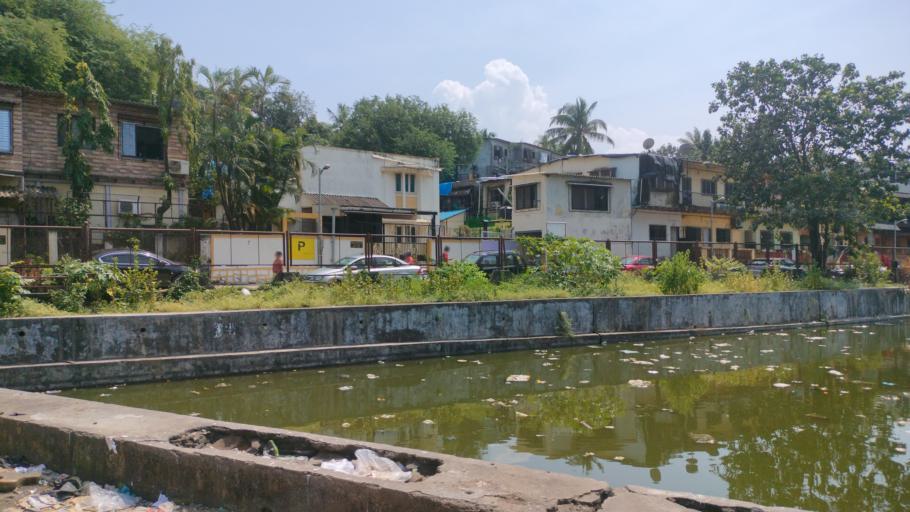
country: IN
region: Maharashtra
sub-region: Mumbai Suburban
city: Borivli
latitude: 19.1961
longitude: 72.8064
